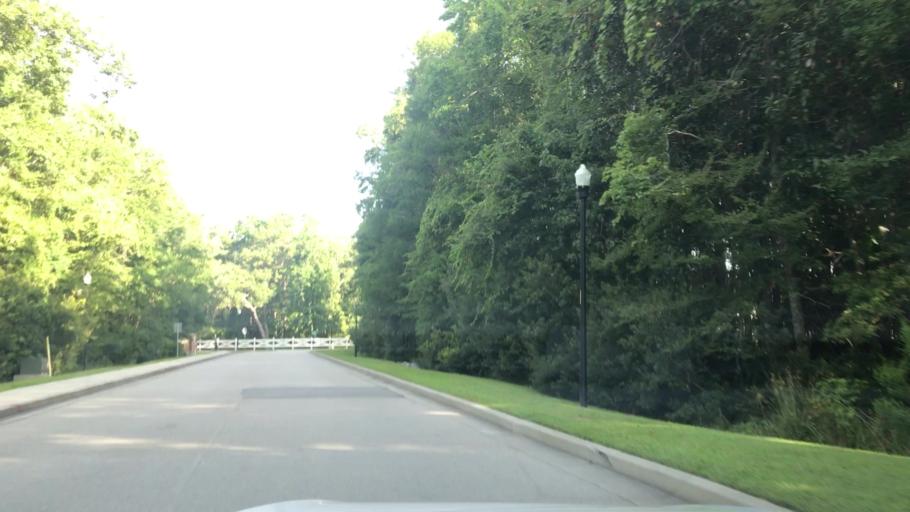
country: US
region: South Carolina
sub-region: Charleston County
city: Isle of Palms
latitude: 32.8904
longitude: -79.7491
